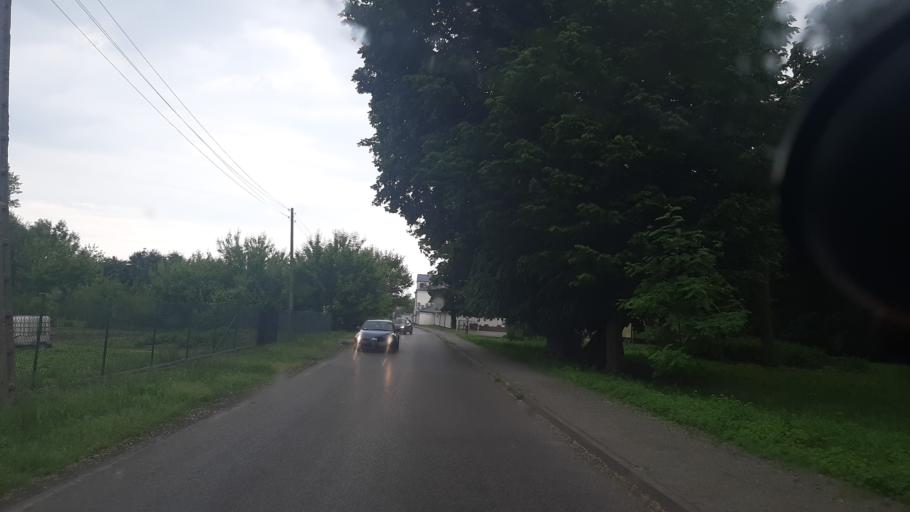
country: PL
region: Lublin Voivodeship
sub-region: Powiat lubelski
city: Garbow
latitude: 51.3558
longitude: 22.3309
